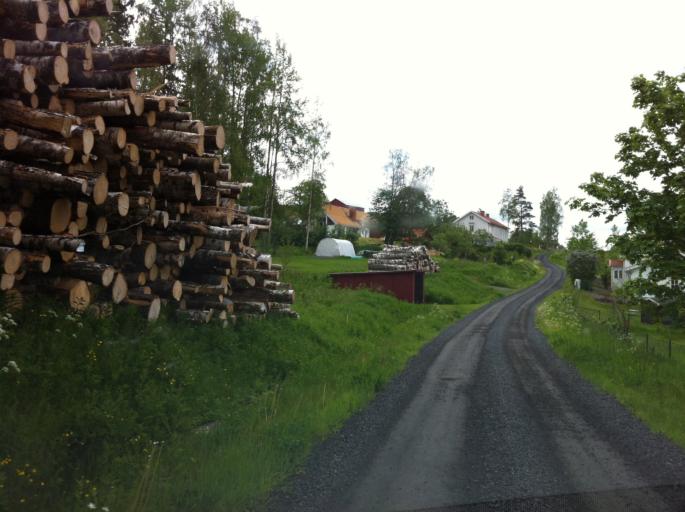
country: SE
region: Vaermland
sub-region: Sunne Kommun
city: Sunne
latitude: 59.9113
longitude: 13.1652
